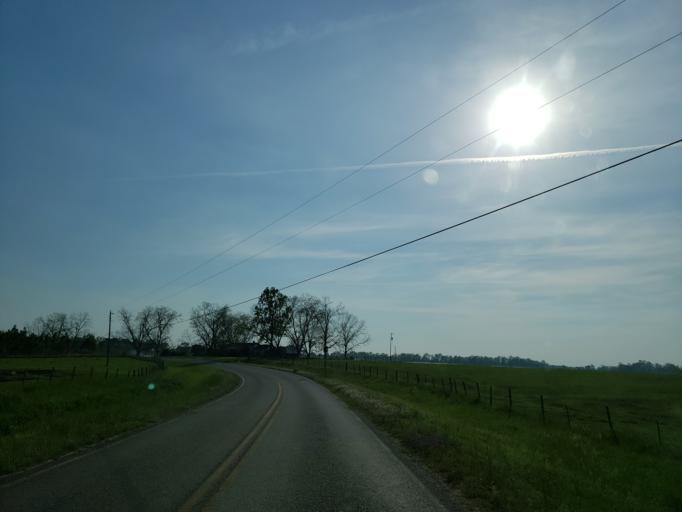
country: US
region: Georgia
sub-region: Tift County
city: Tifton
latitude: 31.5320
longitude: -83.5584
